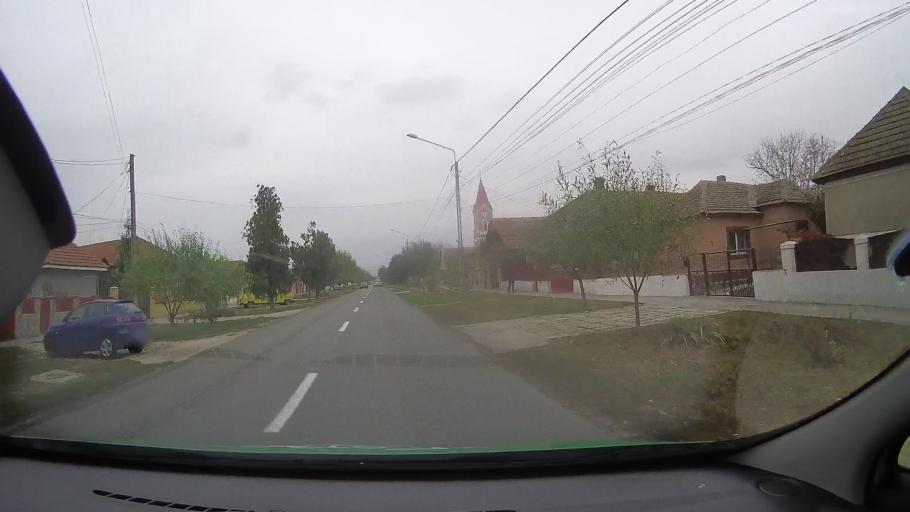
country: RO
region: Constanta
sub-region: Comuna Mihail Kogalniceanu
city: Mihail Kogalniceanu
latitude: 44.3721
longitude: 28.4639
